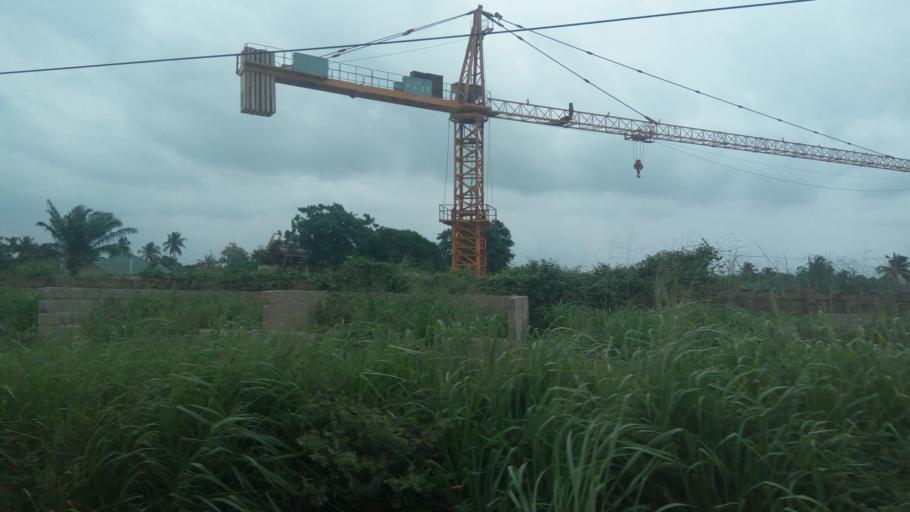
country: TG
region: Maritime
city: Lome
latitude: 6.1143
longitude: 1.1282
